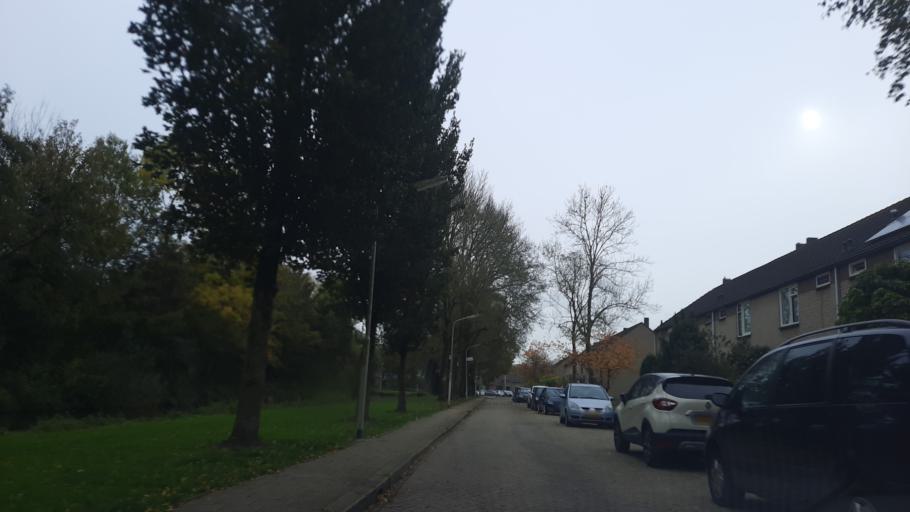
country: NL
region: South Holland
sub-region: Gemeente Gorinchem
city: Gorinchem
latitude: 51.8444
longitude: 4.9579
